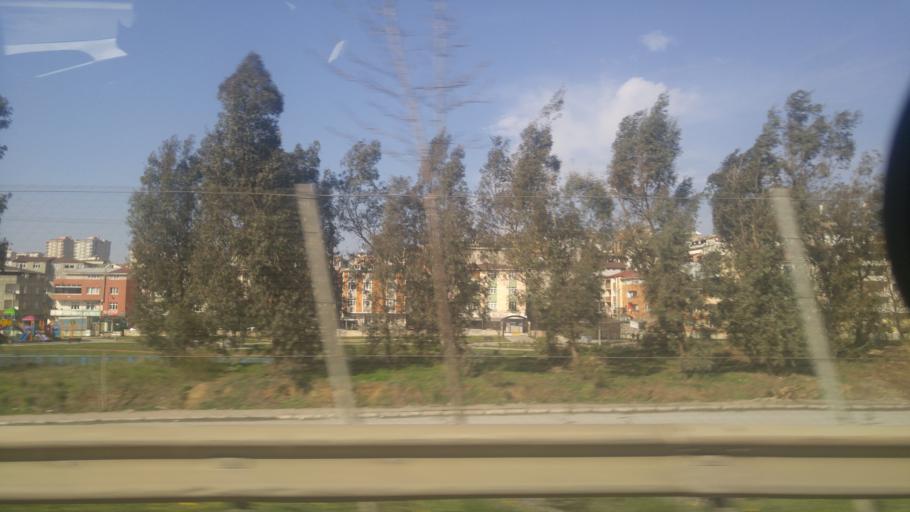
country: TR
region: Kocaeli
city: Darica
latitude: 40.8282
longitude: 29.3660
